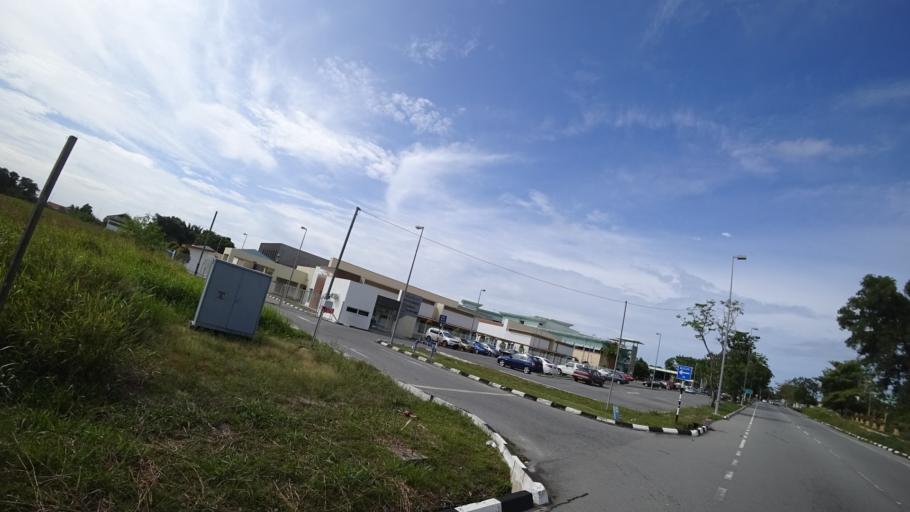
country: BN
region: Tutong
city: Tutong
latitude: 4.8154
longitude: 114.6635
